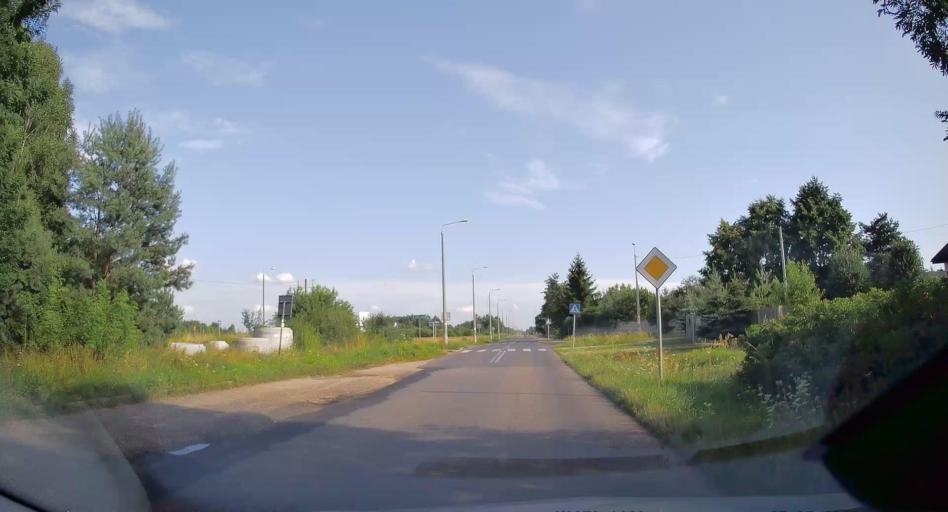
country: PL
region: Swietokrzyskie
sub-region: Powiat konecki
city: Konskie
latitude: 51.2180
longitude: 20.3903
